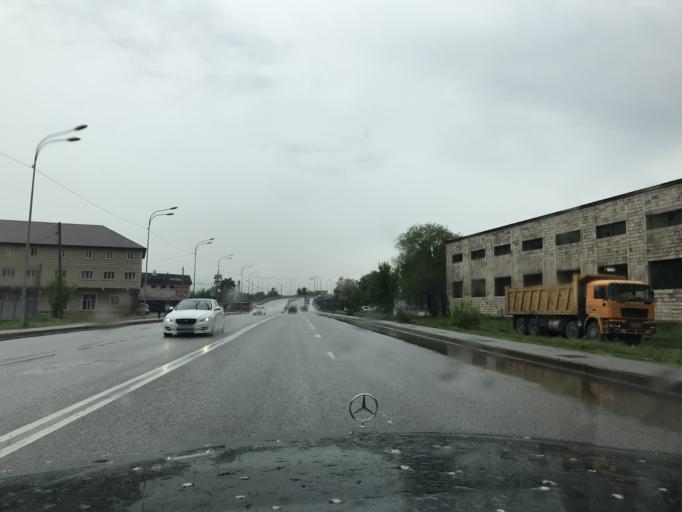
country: KZ
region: Almaty Oblysy
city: Pervomayskiy
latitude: 43.3414
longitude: 76.9665
